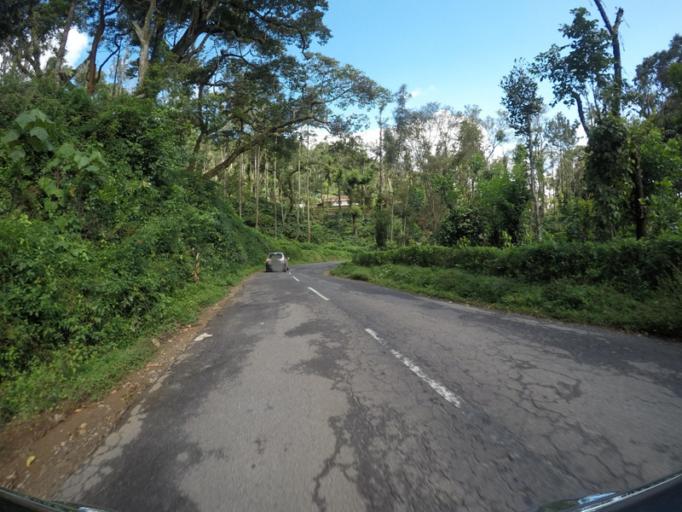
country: IN
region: Karnataka
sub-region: Kodagu
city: Suntikoppa
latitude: 12.4783
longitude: 75.7899
